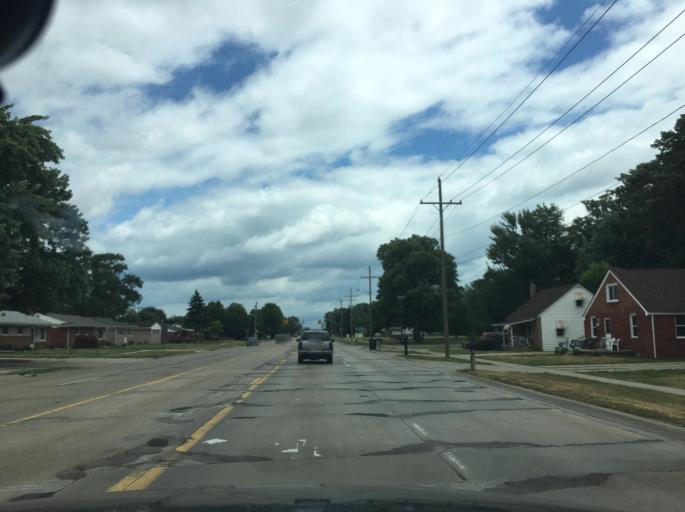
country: US
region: Michigan
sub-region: Macomb County
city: Fraser
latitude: 42.5244
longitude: -82.9314
